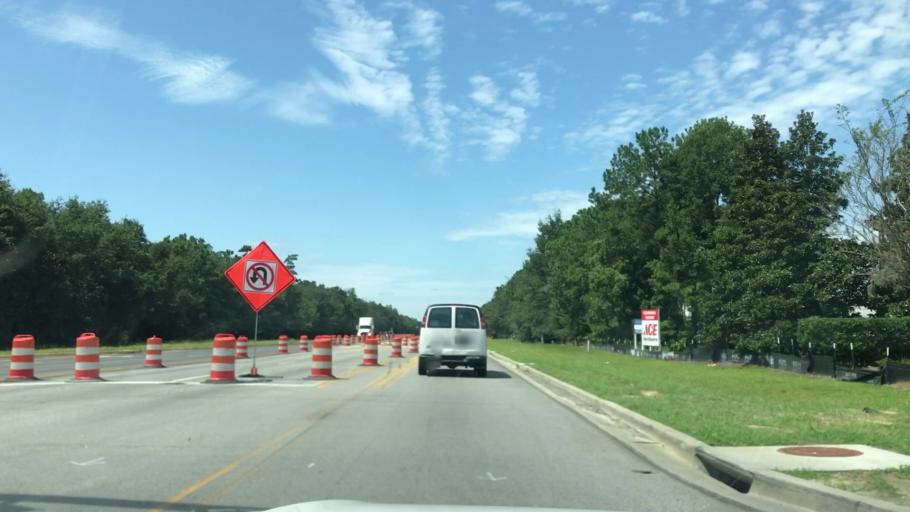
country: US
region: South Carolina
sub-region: Charleston County
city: North Charleston
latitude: 32.9074
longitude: -79.9045
